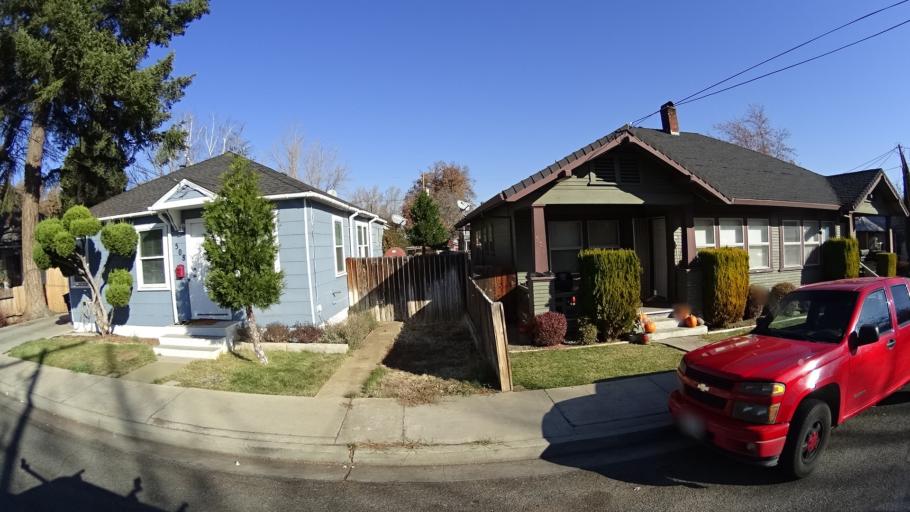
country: US
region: California
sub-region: Siskiyou County
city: Yreka
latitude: 41.7311
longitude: -122.6404
